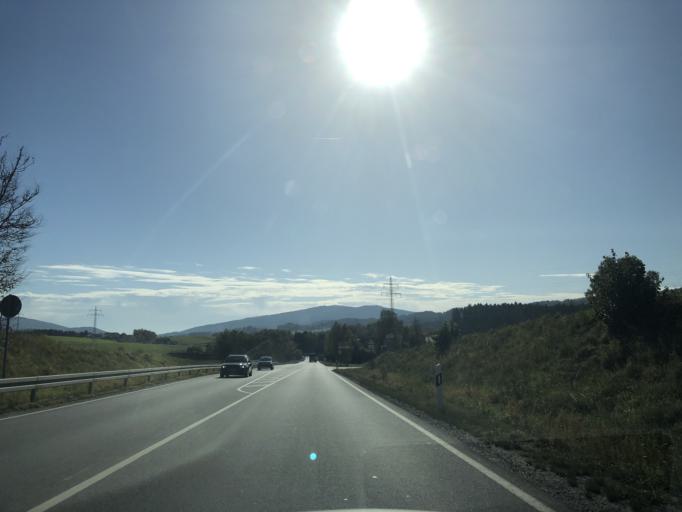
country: DE
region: Bavaria
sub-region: Lower Bavaria
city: Patersdorf
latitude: 49.0042
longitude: 12.9821
